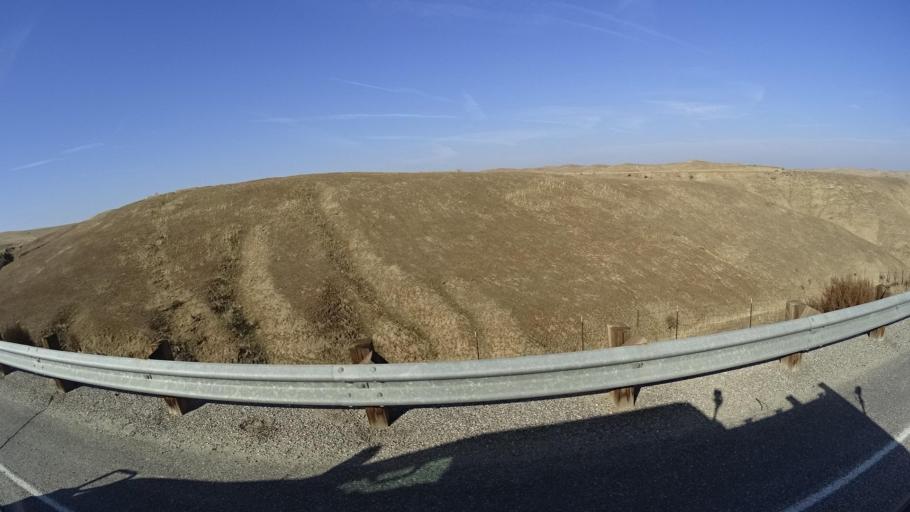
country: US
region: California
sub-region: Kern County
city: Oildale
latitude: 35.5253
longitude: -118.9768
